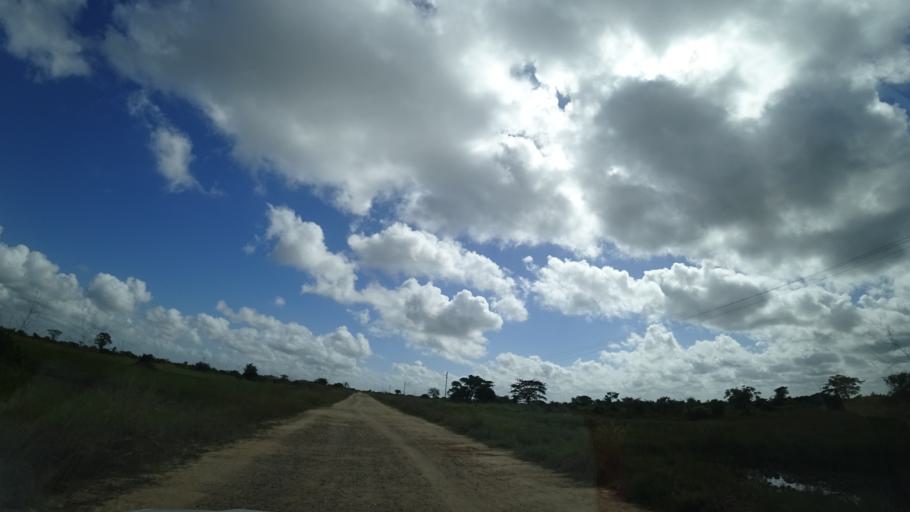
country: MZ
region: Sofala
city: Dondo
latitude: -19.4374
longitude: 34.5614
